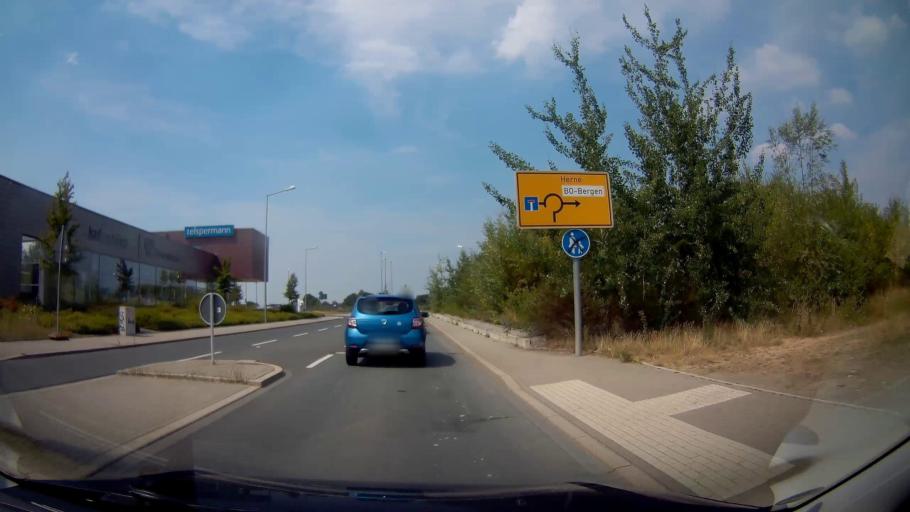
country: DE
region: North Rhine-Westphalia
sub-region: Regierungsbezirk Arnsberg
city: Herne
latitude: 51.5091
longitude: 7.2559
